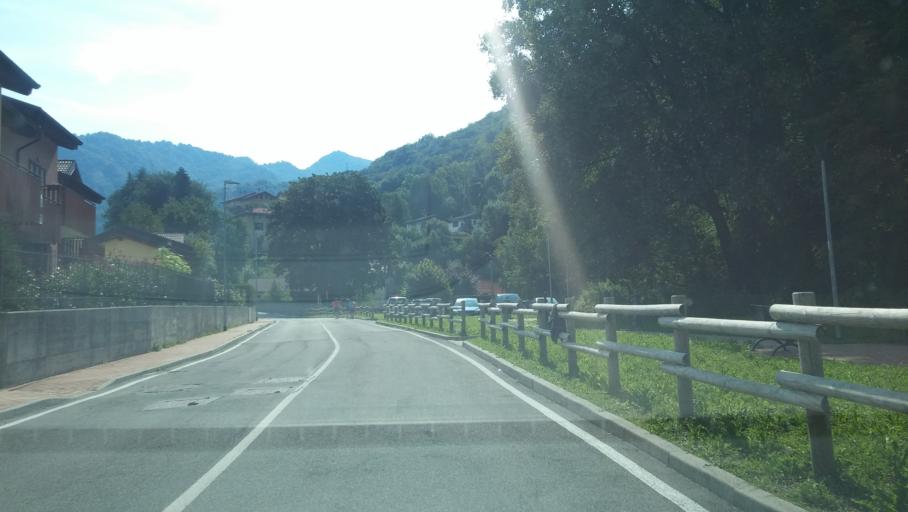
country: IT
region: Lombardy
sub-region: Provincia di Lecco
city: Cremeno
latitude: 45.9218
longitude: 9.4502
